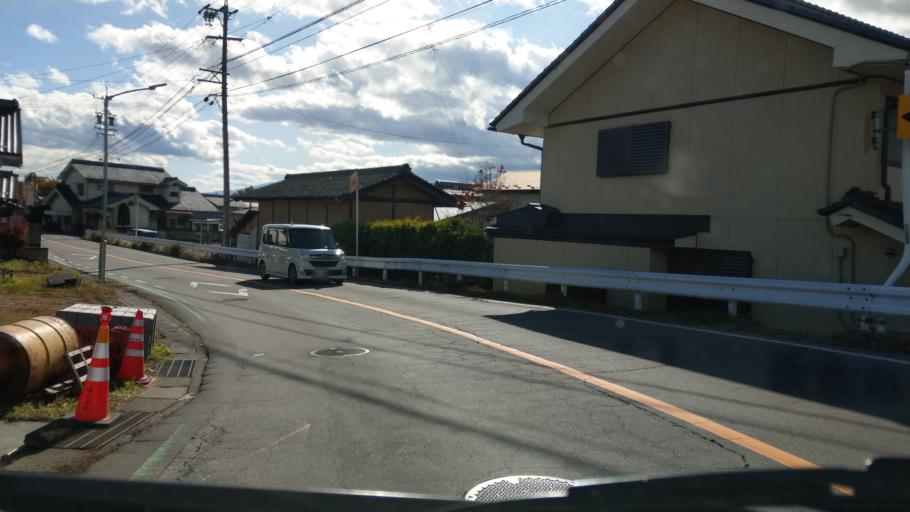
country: JP
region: Nagano
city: Komoro
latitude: 36.3100
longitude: 138.4271
